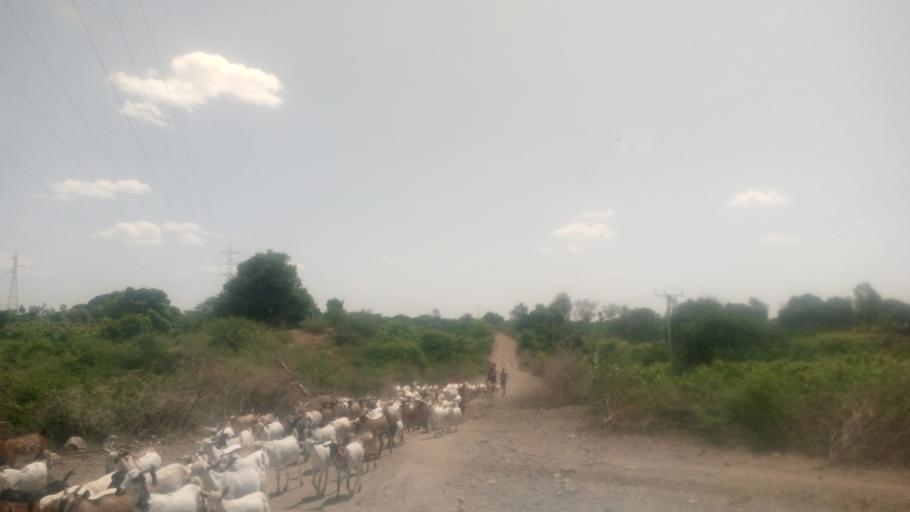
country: ET
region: Oromiya
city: Deder
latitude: 9.5285
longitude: 41.3522
